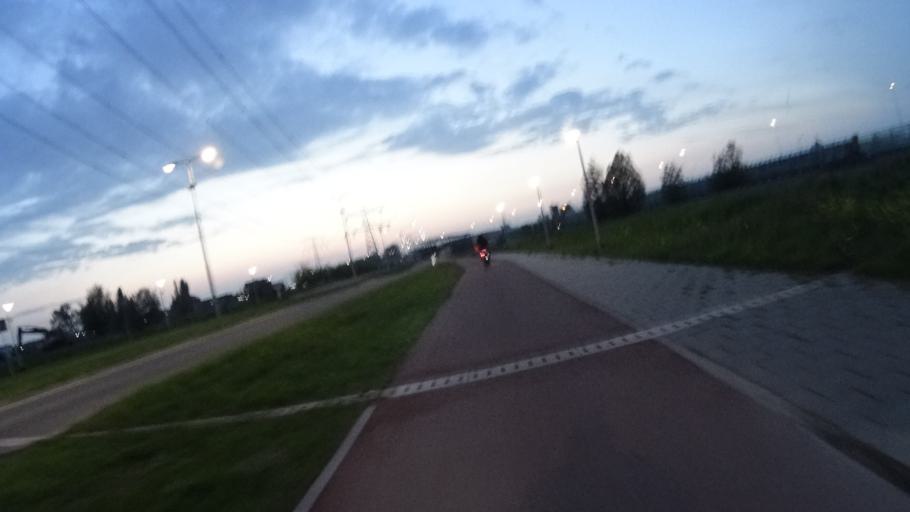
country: NL
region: South Holland
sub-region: Gemeente Sliedrecht
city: Sliedrecht
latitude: 51.8319
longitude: 4.7370
